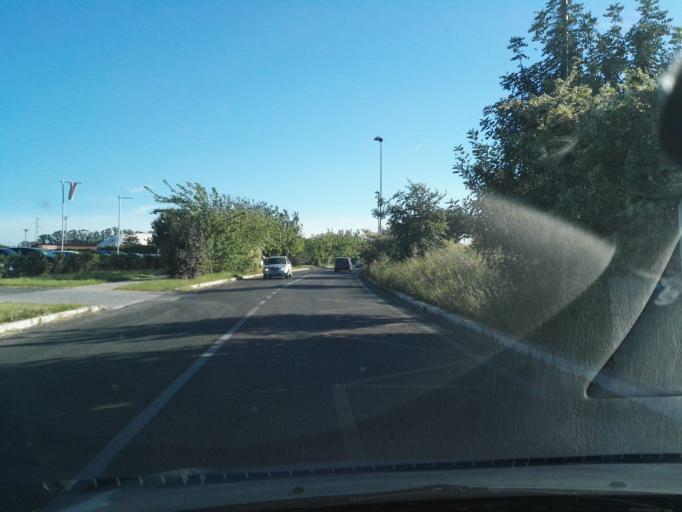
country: IT
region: Latium
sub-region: Citta metropolitana di Roma Capitale
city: Selcetta
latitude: 41.7828
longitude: 12.4767
